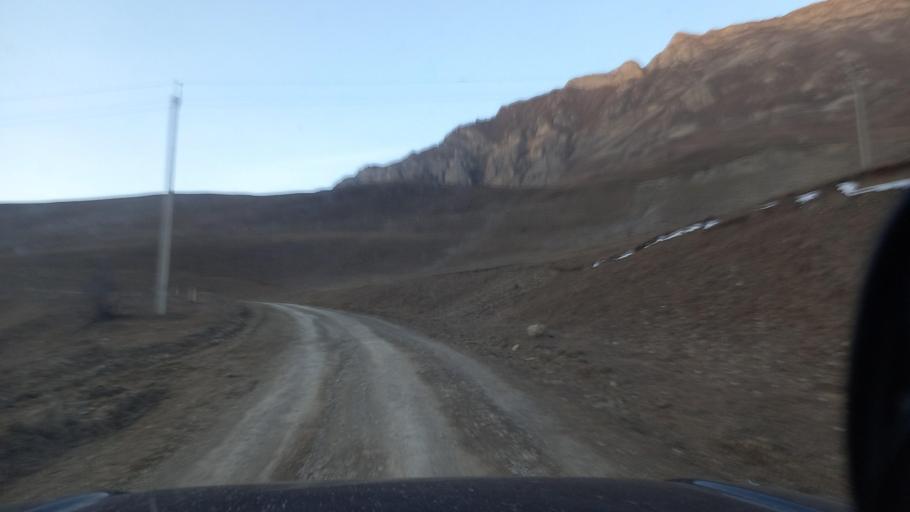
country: RU
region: Ingushetiya
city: Dzhayrakh
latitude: 42.8381
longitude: 44.5424
